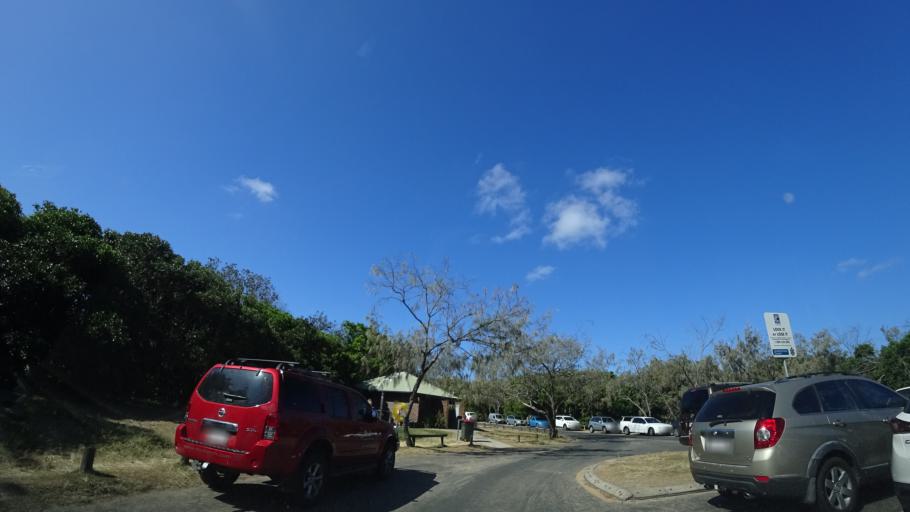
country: AU
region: Queensland
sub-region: Sunshine Coast
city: Mooloolaba
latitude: -26.6392
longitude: 153.1003
